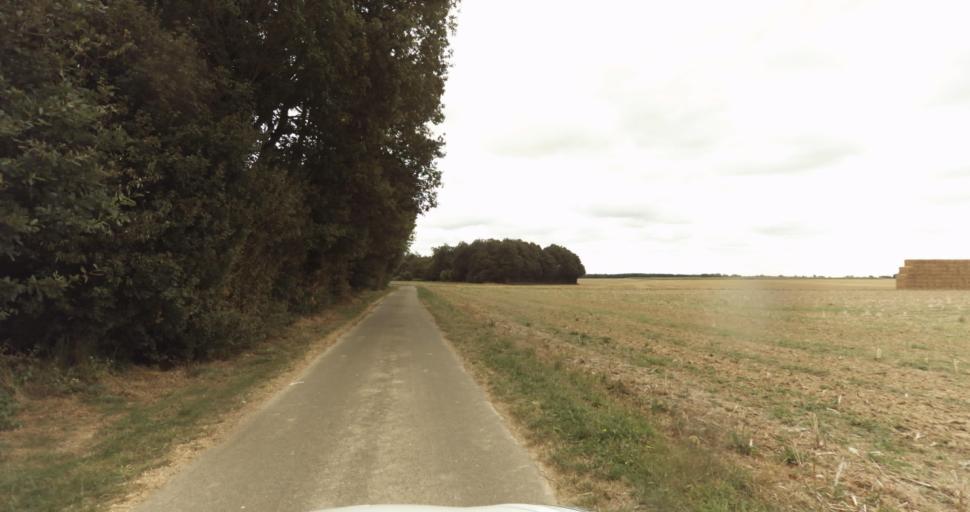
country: FR
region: Haute-Normandie
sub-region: Departement de l'Eure
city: Nonancourt
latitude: 48.8155
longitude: 1.1576
